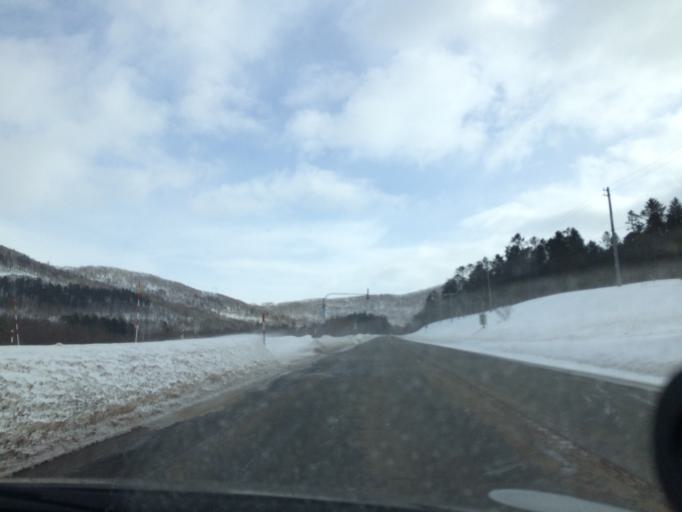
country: JP
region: Hokkaido
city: Shimo-furano
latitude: 43.1362
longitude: 142.7546
